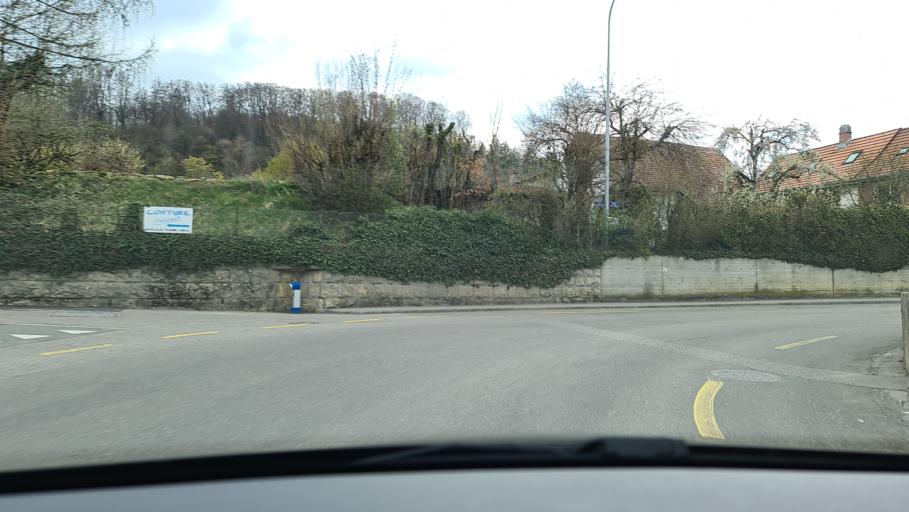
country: CH
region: Jura
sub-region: Porrentruy District
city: Porrentruy
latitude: 47.4554
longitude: 7.0486
